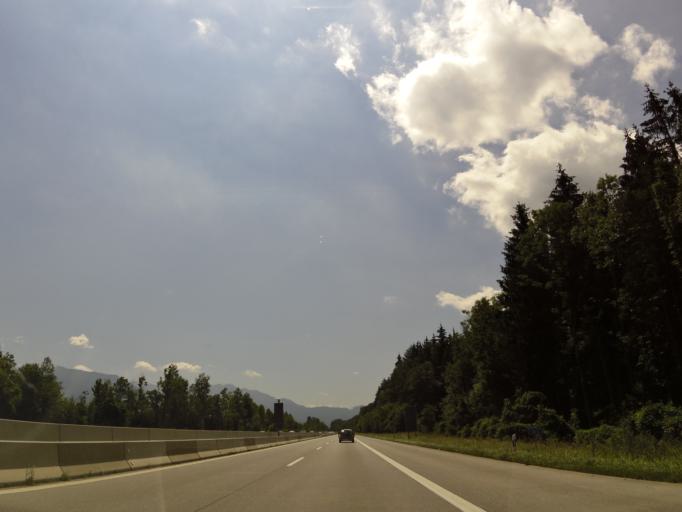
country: AT
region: Tyrol
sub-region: Politischer Bezirk Kufstein
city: Erl
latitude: 47.6936
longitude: 12.1626
